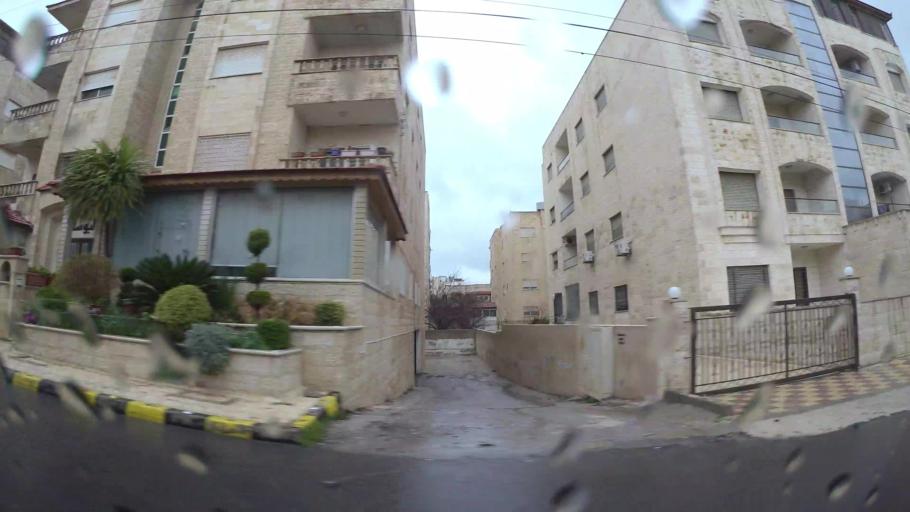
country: JO
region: Amman
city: Al Jubayhah
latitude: 32.0250
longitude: 35.8734
